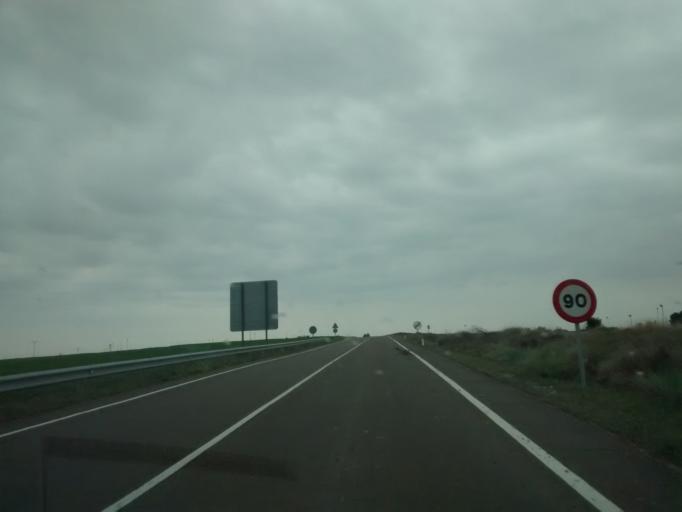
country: ES
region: Aragon
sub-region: Provincia de Zaragoza
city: Bujaraloz
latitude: 41.5180
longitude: -0.1743
